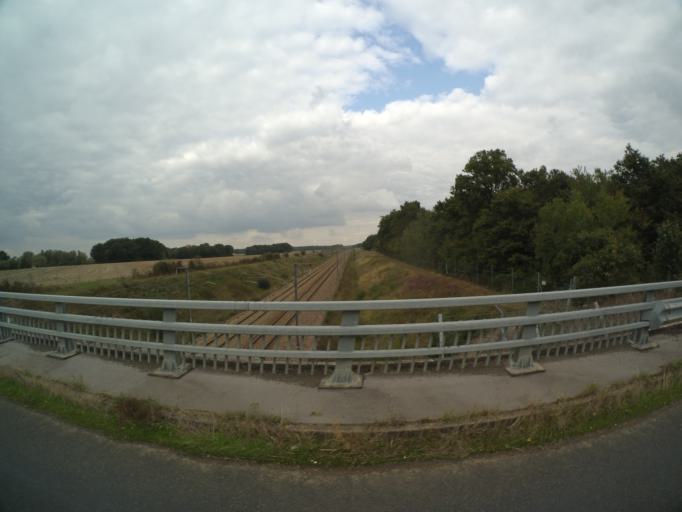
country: FR
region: Centre
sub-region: Departement d'Indre-et-Loire
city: Auzouer-en-Touraine
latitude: 47.5158
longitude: 0.9535
